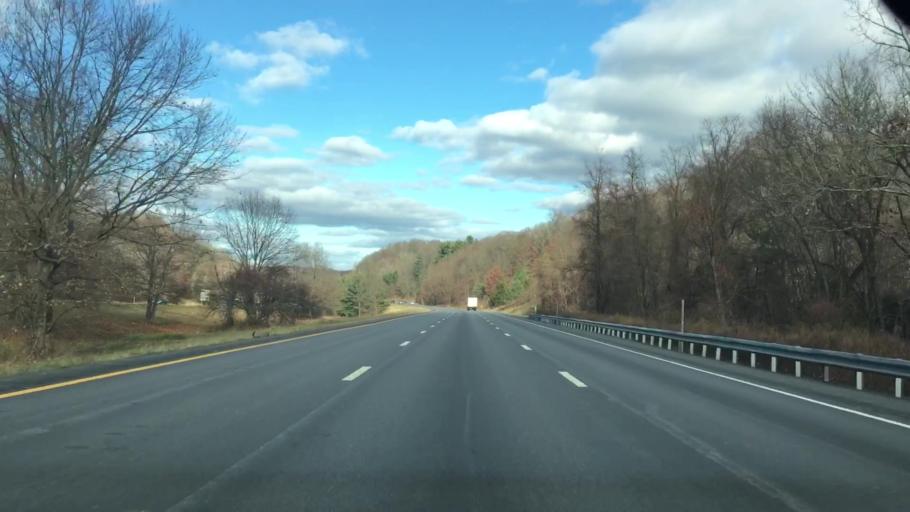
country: US
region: New York
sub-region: Westchester County
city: Bedford Hills
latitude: 41.2337
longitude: -73.6782
